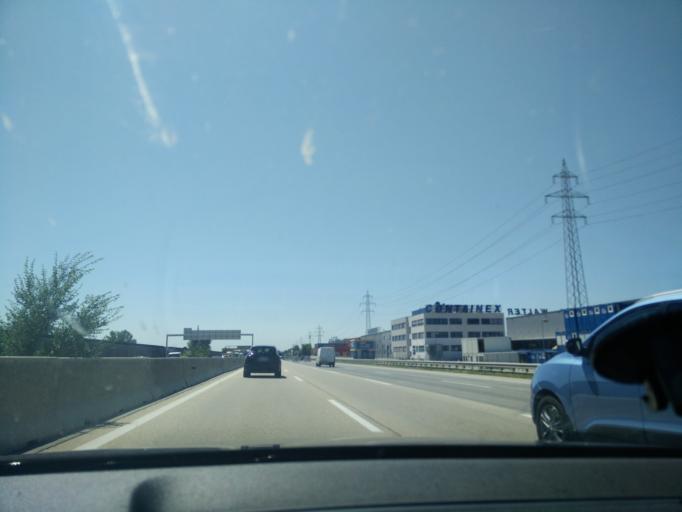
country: AT
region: Lower Austria
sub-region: Politischer Bezirk Modling
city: Biedermannsdorf
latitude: 48.0682
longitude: 16.3388
